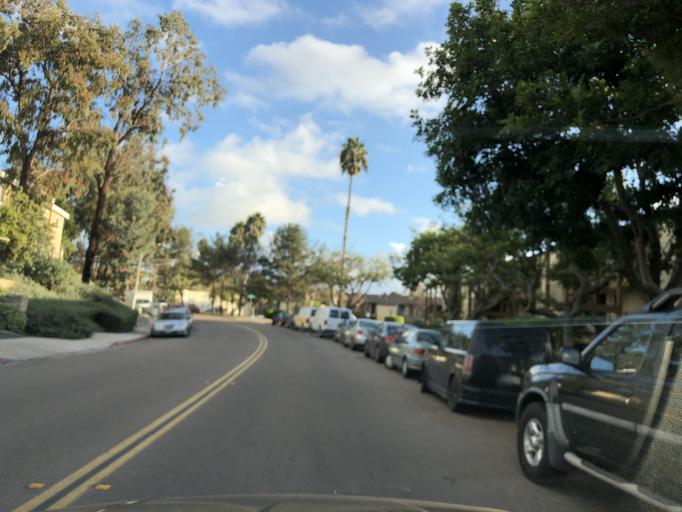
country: US
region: California
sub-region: San Diego County
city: La Jolla
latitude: 32.8176
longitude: -117.1774
